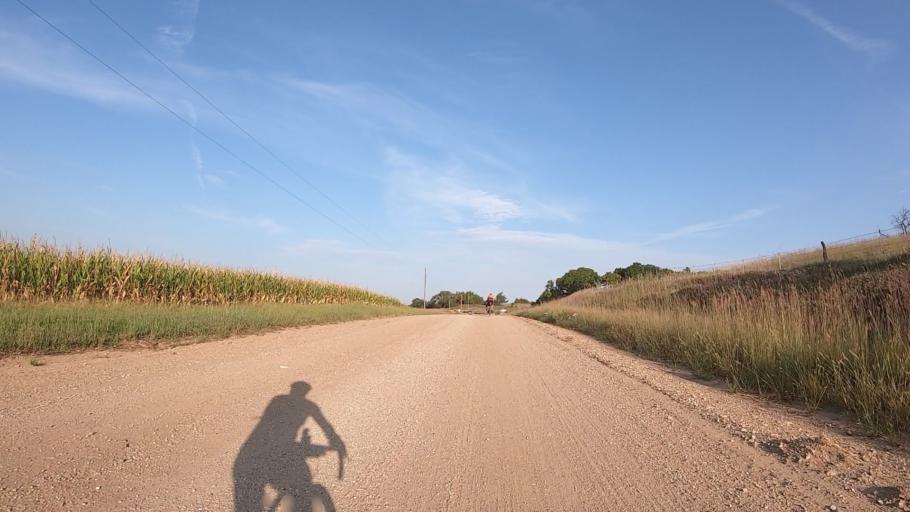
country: US
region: Kansas
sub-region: Marshall County
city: Blue Rapids
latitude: 39.7251
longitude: -96.7858
